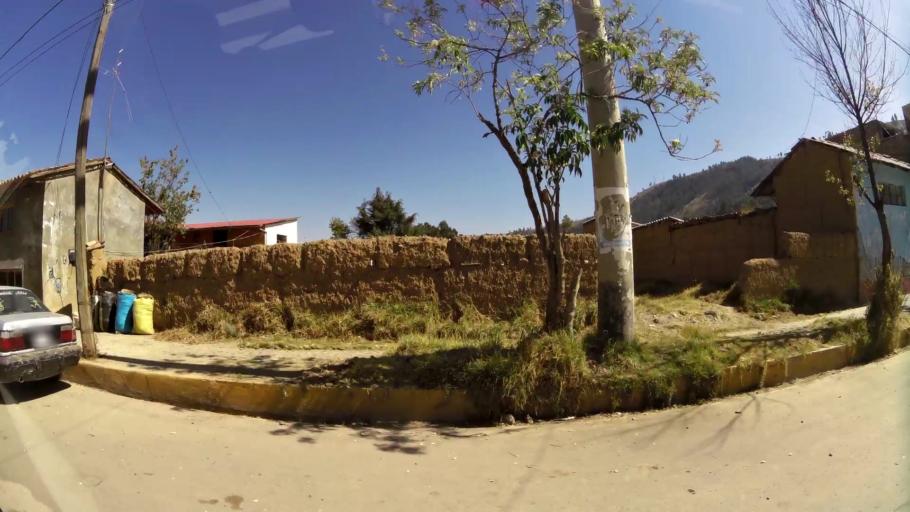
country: PE
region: Junin
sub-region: Provincia de Huancayo
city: San Jeronimo
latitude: -11.9430
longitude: -75.2941
